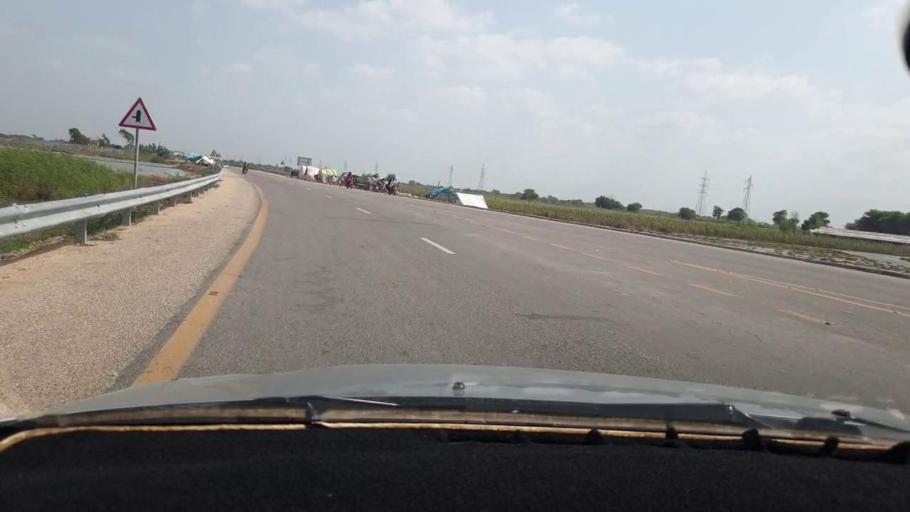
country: PK
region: Sindh
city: Digri
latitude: 25.0518
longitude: 69.2227
